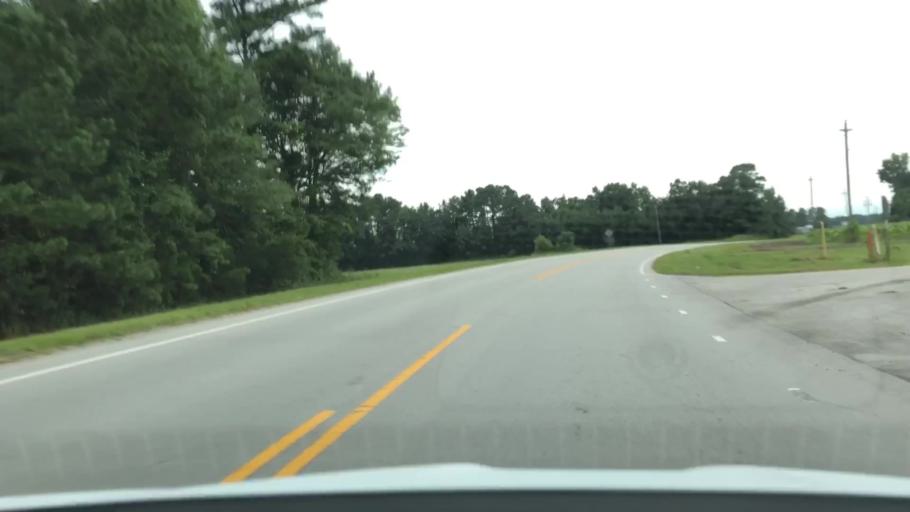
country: US
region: North Carolina
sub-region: Jones County
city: Trenton
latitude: 35.0403
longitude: -77.3494
